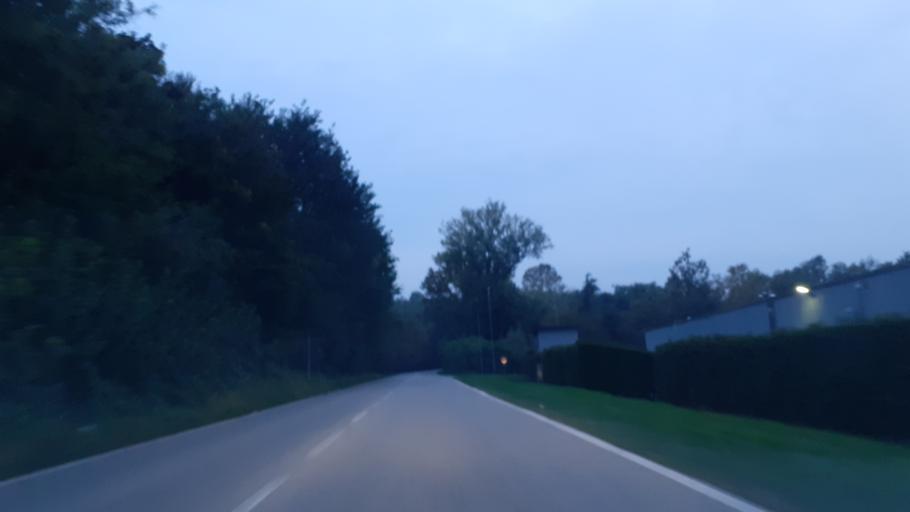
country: IT
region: Lombardy
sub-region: Provincia di Lecco
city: Garbagnate
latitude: 45.7652
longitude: 9.2969
